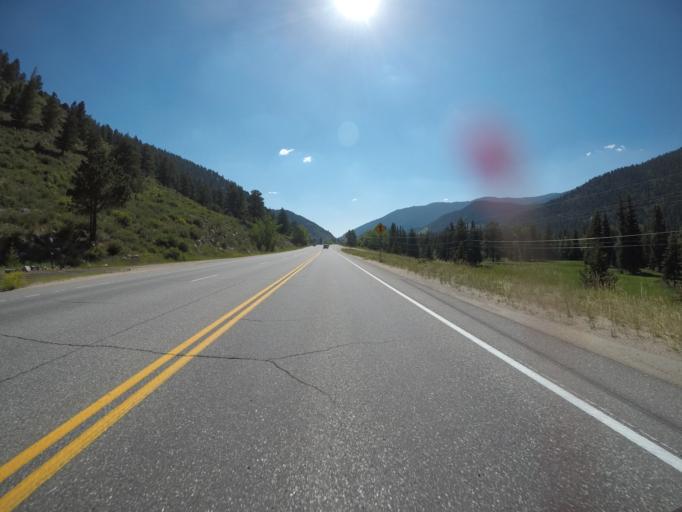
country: US
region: Colorado
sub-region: Clear Creek County
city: Georgetown
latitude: 39.7613
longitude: -105.6980
